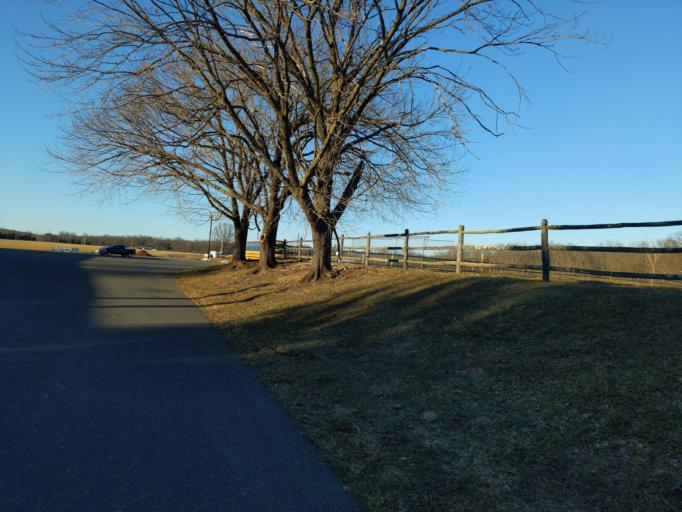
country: US
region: Pennsylvania
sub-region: Bucks County
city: Spinnerstown
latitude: 40.4443
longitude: -75.3988
